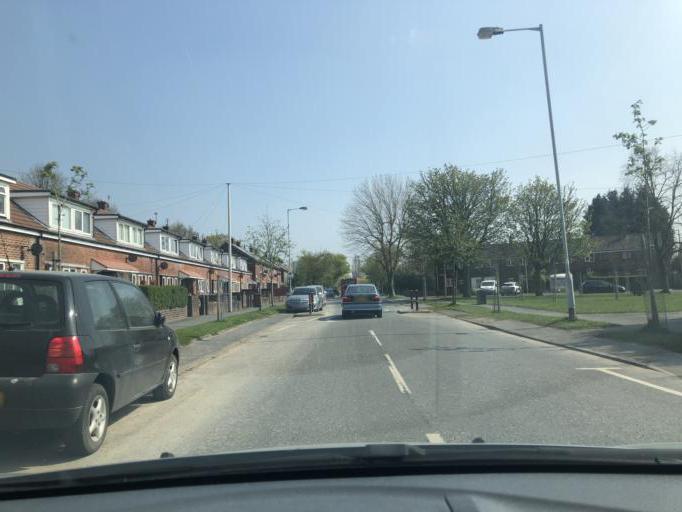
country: GB
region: England
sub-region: Borough of Stockport
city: Bredbury
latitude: 53.4313
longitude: -2.1336
